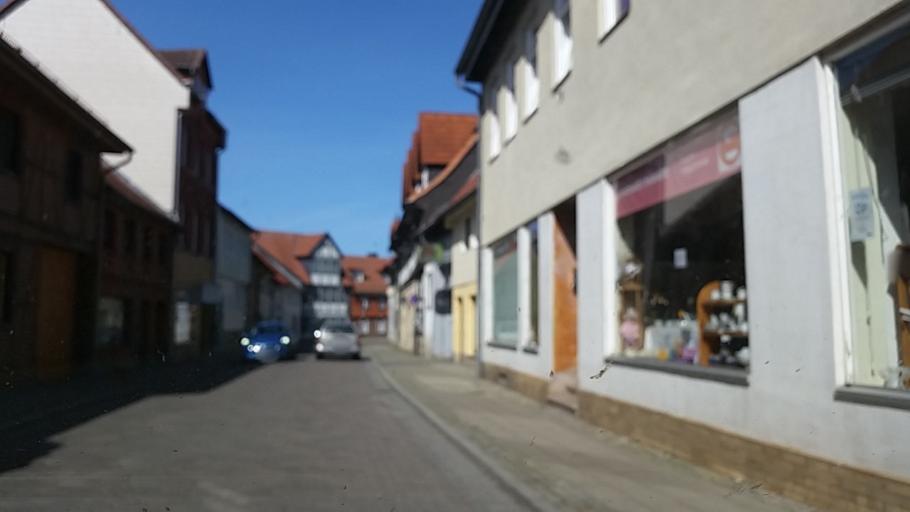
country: DE
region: Lower Saxony
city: Schoppenstedt
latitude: 52.1455
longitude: 10.7748
